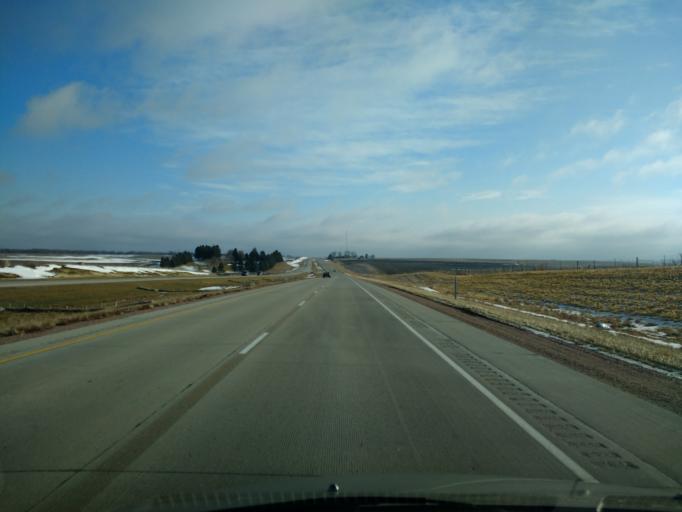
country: US
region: Iowa
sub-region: Ida County
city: Holstein
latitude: 42.4743
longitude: -95.5696
